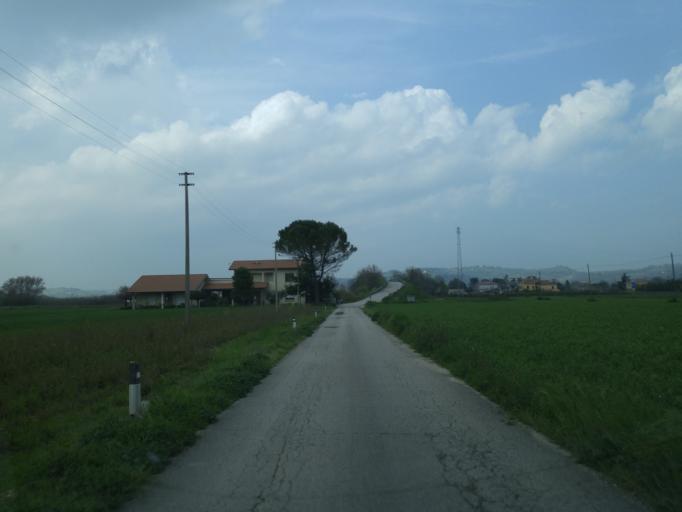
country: IT
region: The Marches
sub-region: Provincia di Pesaro e Urbino
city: Bellocchi
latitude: 43.7817
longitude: 12.9931
